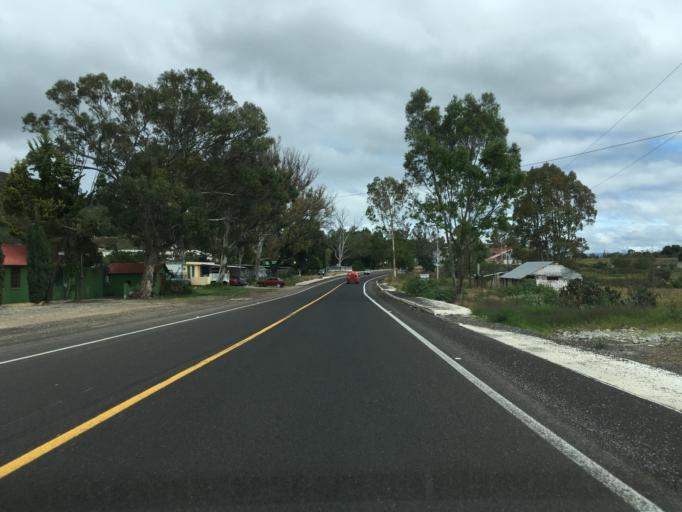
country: MX
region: Hidalgo
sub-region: Atotonilco el Grande
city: Santa Maria Amajac
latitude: 20.4044
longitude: -98.7133
